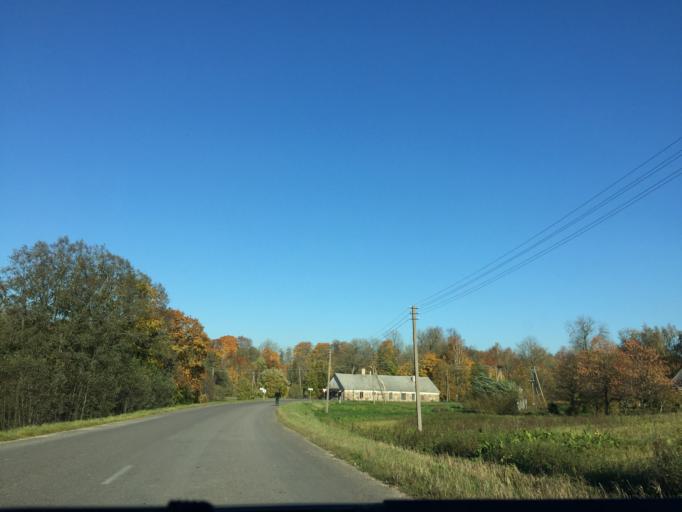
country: LT
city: Plateliai
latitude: 56.0474
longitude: 21.7235
